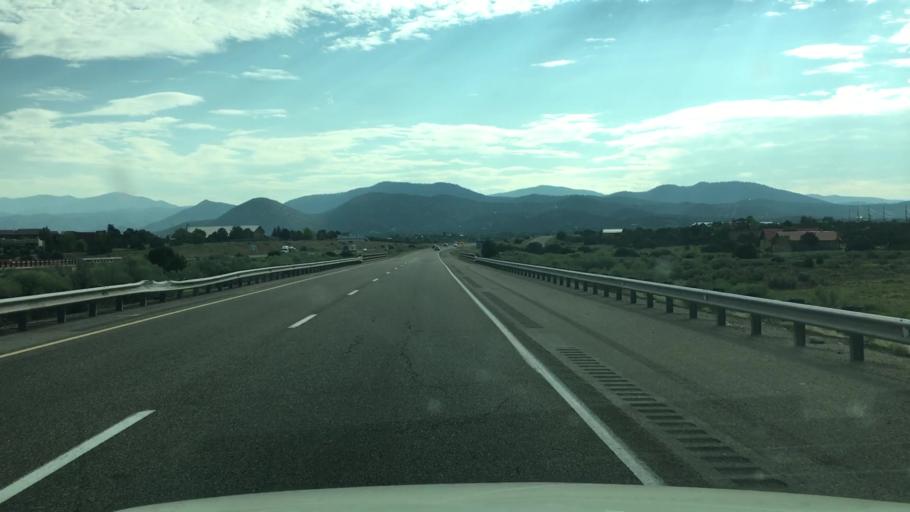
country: US
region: New Mexico
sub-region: Santa Fe County
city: Santa Fe
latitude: 35.6345
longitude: -105.9556
